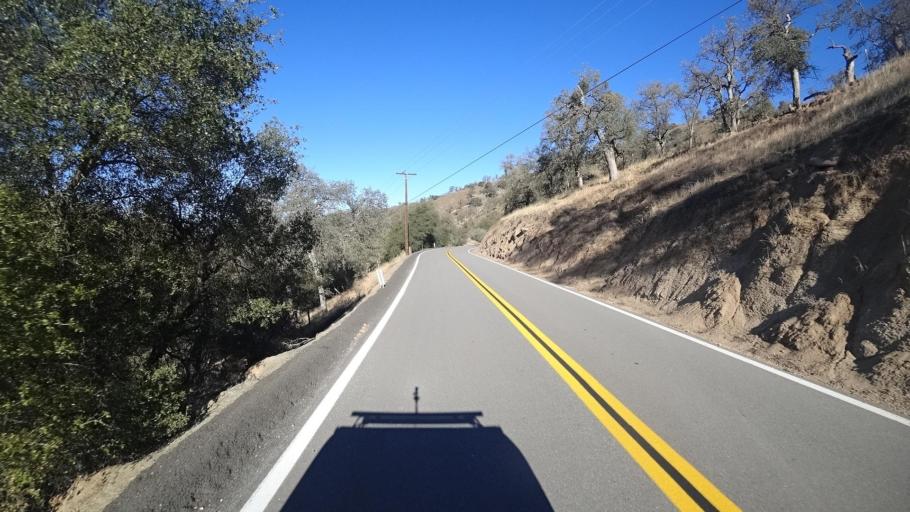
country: US
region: California
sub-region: Kern County
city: Alta Sierra
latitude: 35.7100
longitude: -118.7776
